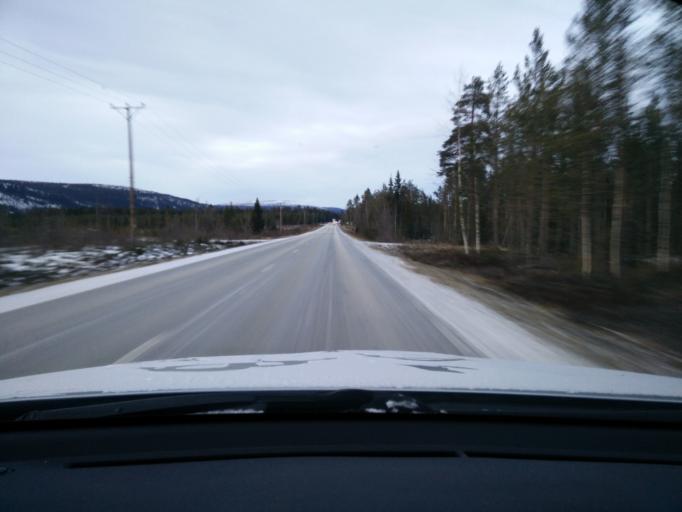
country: SE
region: Jaemtland
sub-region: Bergs Kommun
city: Hoverberg
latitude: 62.4970
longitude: 14.2107
